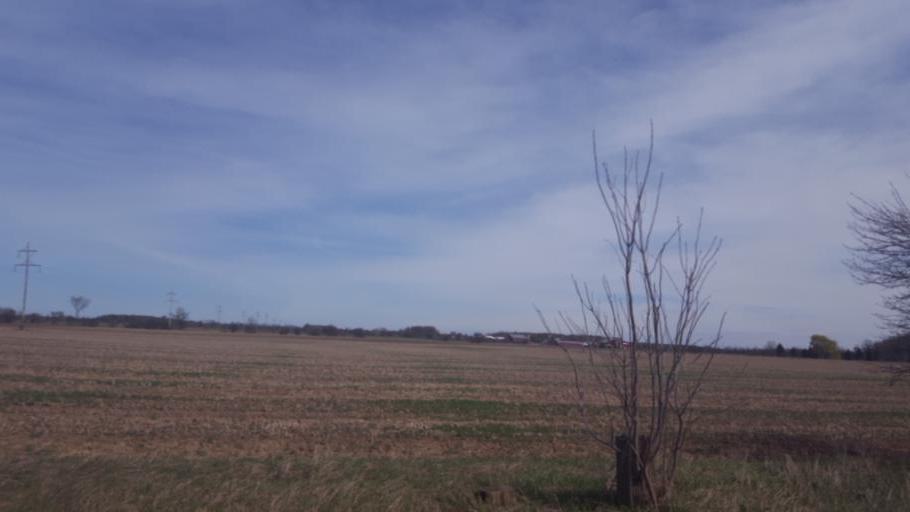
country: US
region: Michigan
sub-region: Gladwin County
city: Gladwin
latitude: 44.0337
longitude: -84.4672
